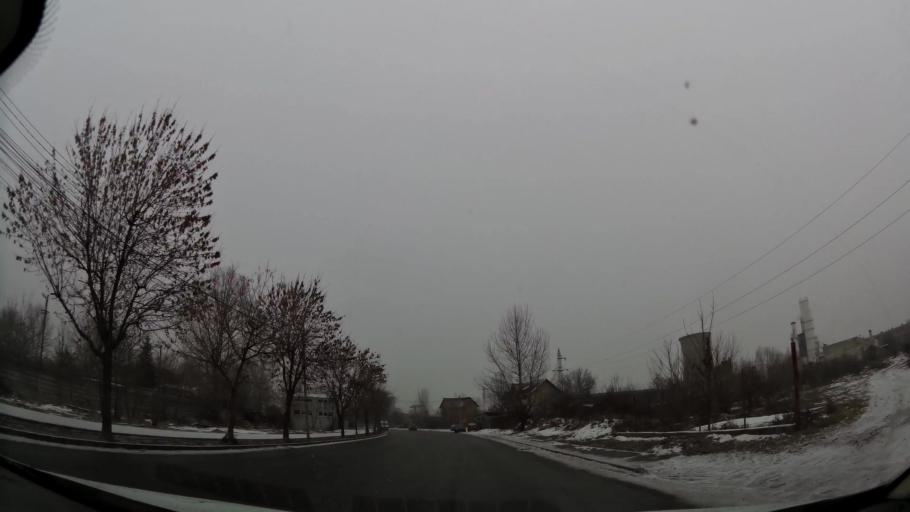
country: RO
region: Dambovita
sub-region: Municipiul Targoviste
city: Targoviste
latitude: 44.9131
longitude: 25.4441
